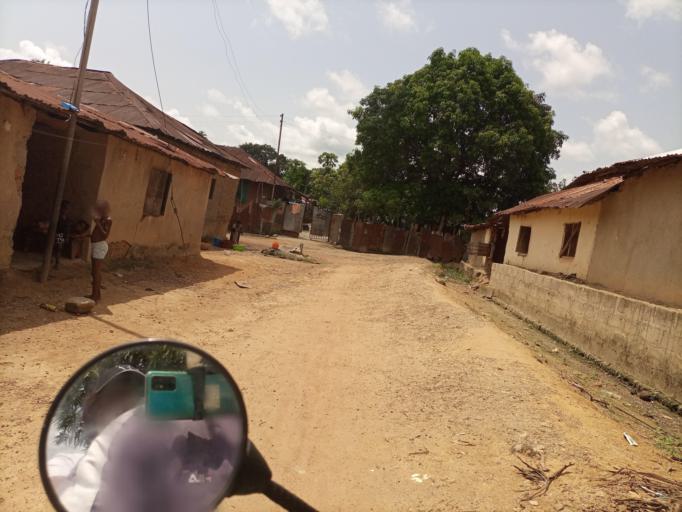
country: SL
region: Southern Province
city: Bo
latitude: 7.9599
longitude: -11.7350
